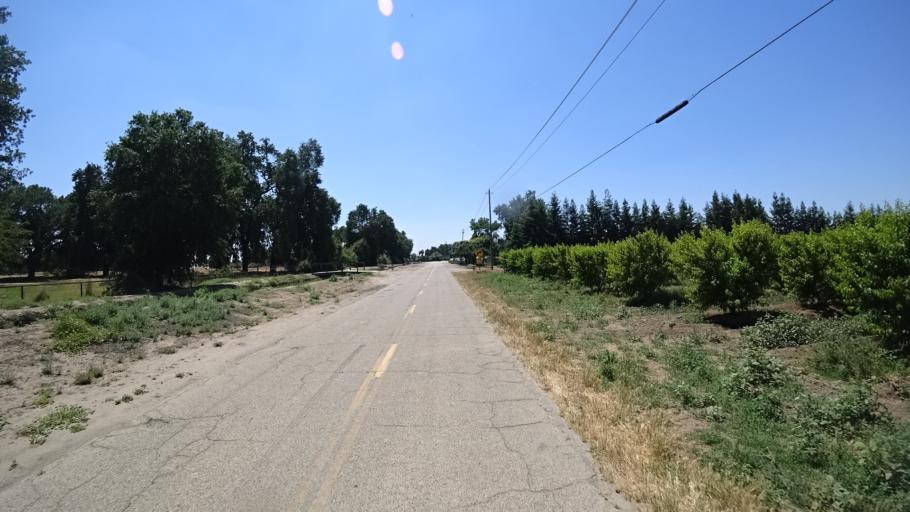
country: US
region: California
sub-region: Fresno County
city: Kingsburg
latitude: 36.4913
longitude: -119.5390
